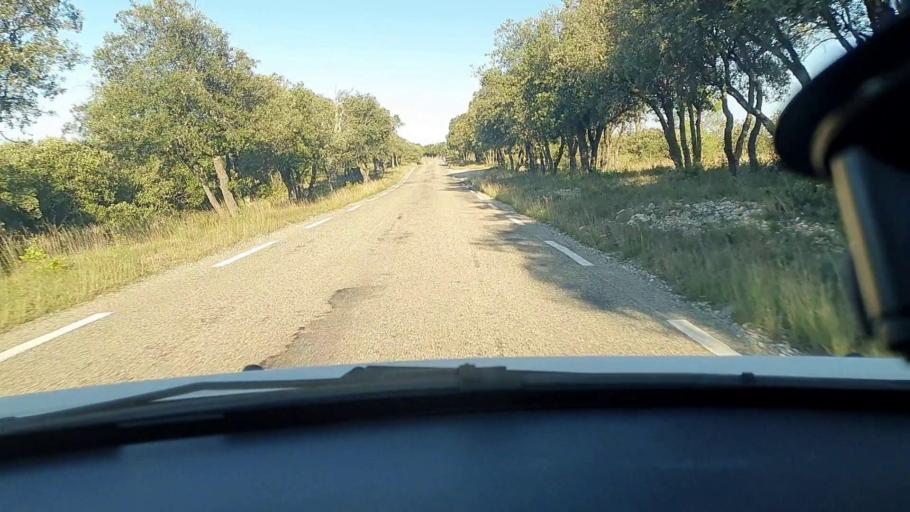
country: FR
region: Languedoc-Roussillon
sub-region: Departement du Gard
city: Goudargues
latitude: 44.1606
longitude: 4.3511
